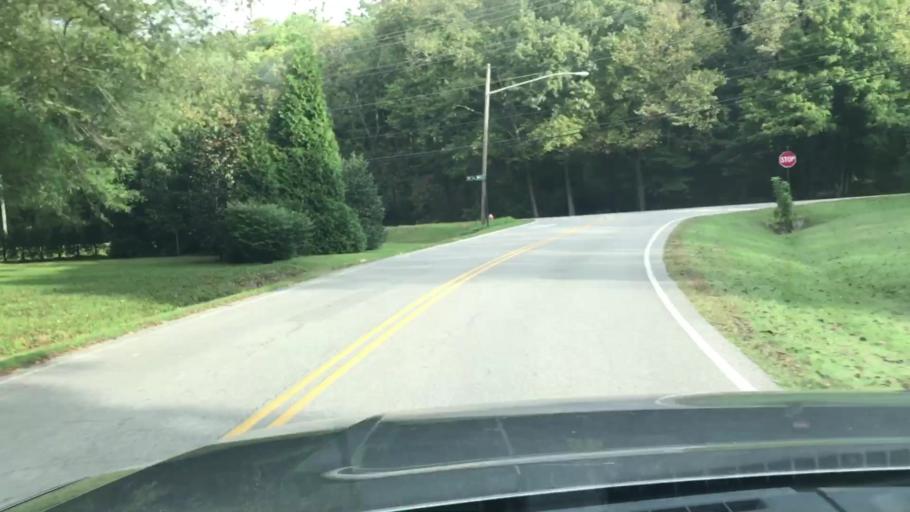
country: US
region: Tennessee
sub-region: Davidson County
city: Forest Hills
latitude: 36.0702
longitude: -86.8289
